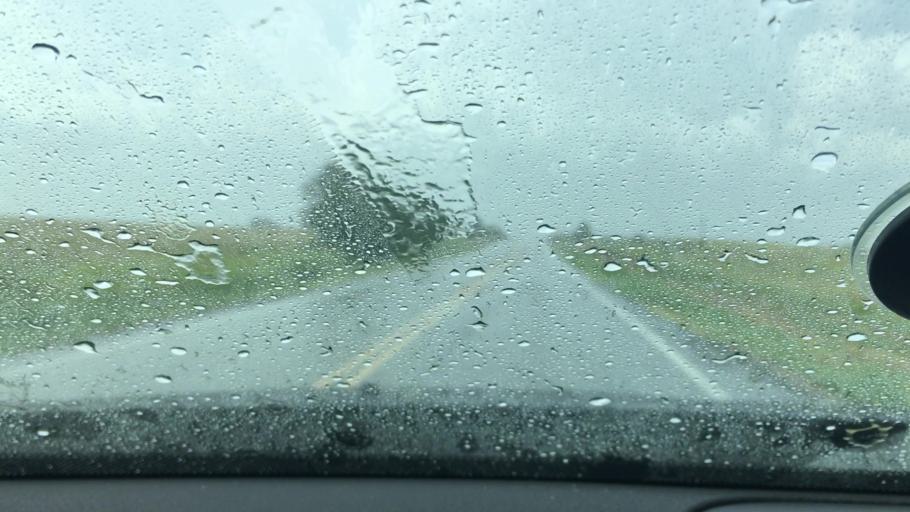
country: US
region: Oklahoma
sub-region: Johnston County
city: Tishomingo
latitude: 34.1658
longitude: -96.7086
